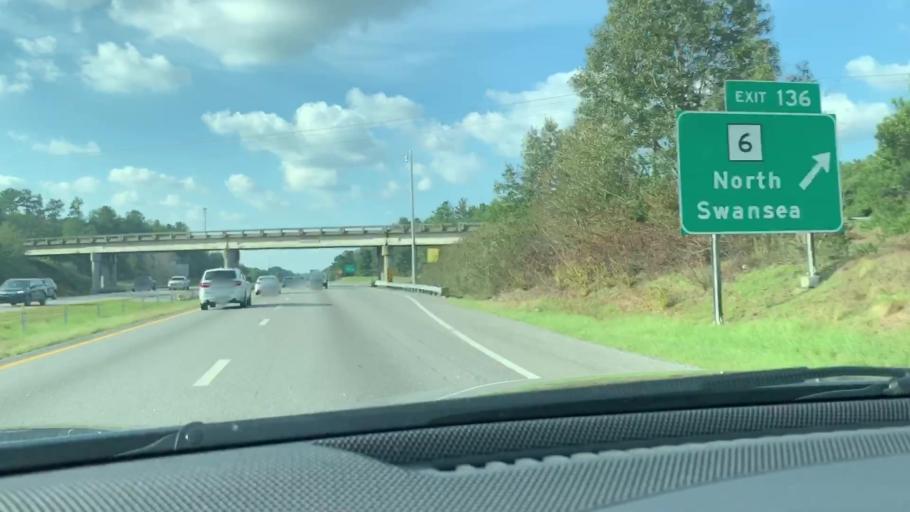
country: US
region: South Carolina
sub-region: Calhoun County
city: Saint Matthews
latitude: 33.6718
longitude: -80.8972
